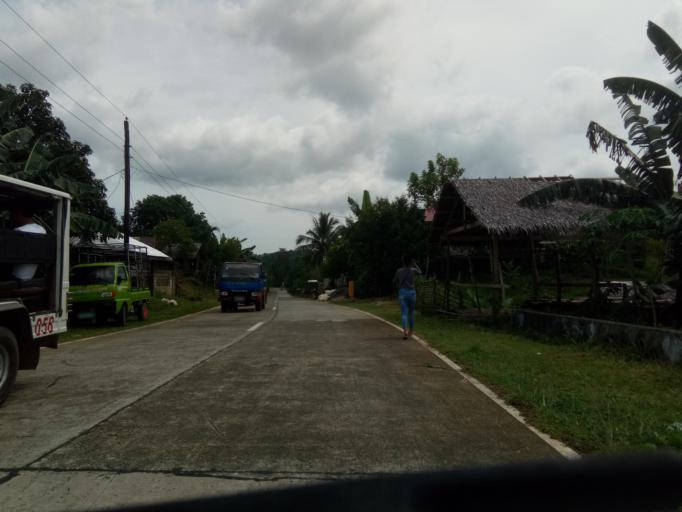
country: PH
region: Caraga
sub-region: Province of Surigao del Norte
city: Pilar
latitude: 9.8905
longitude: 126.0704
